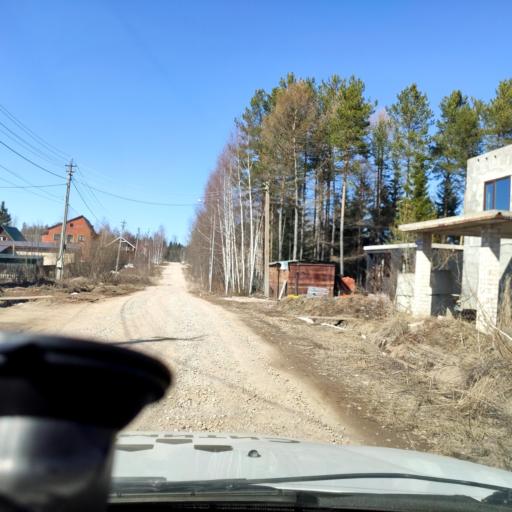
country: RU
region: Perm
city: Ferma
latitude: 57.9288
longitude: 56.4206
